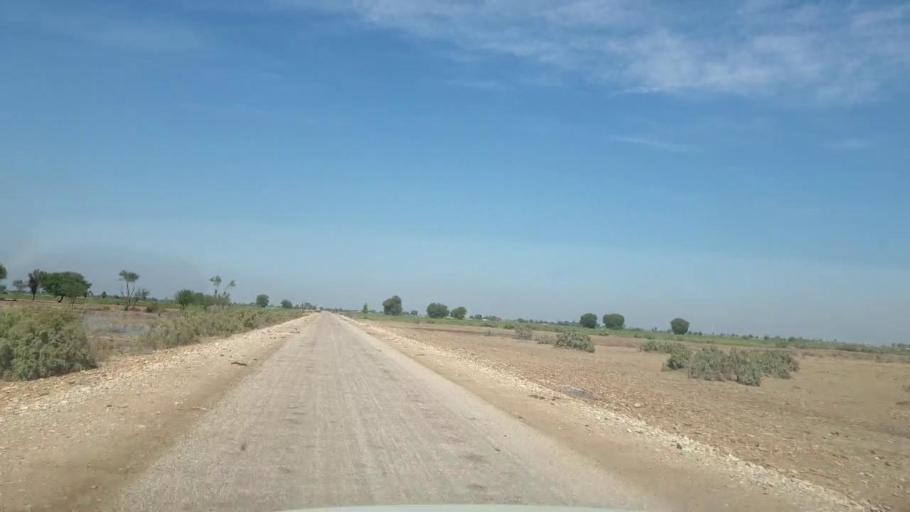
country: PK
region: Sindh
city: Mirpur Khas
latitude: 25.6424
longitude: 69.1939
